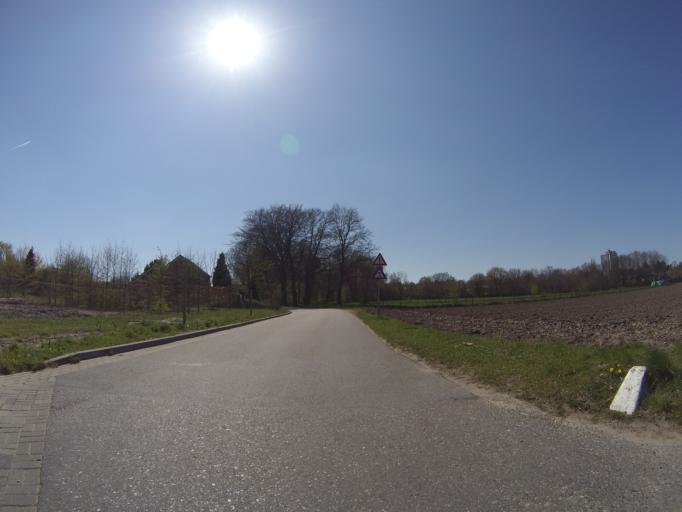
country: NL
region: Utrecht
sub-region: Gemeente Rhenen
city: Rhenen
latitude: 51.9653
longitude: 5.5824
